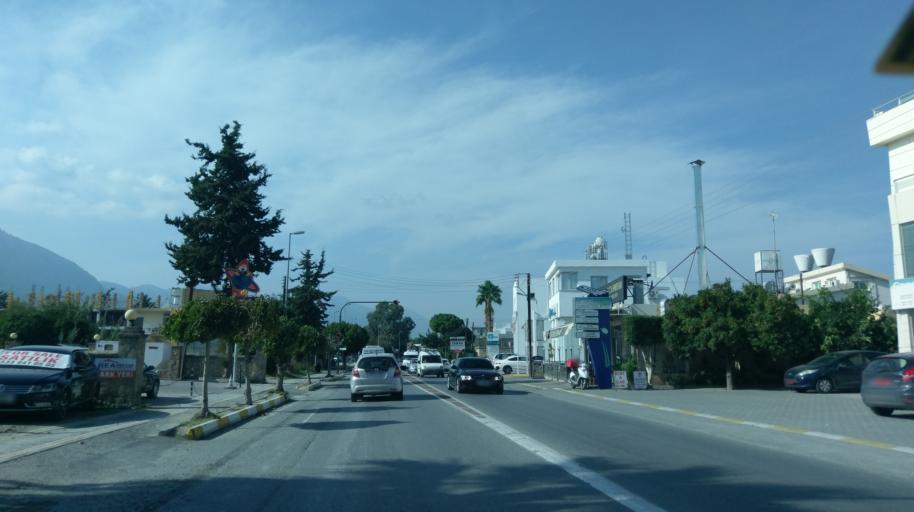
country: CY
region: Keryneia
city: Kyrenia
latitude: 35.3420
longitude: 33.2785
